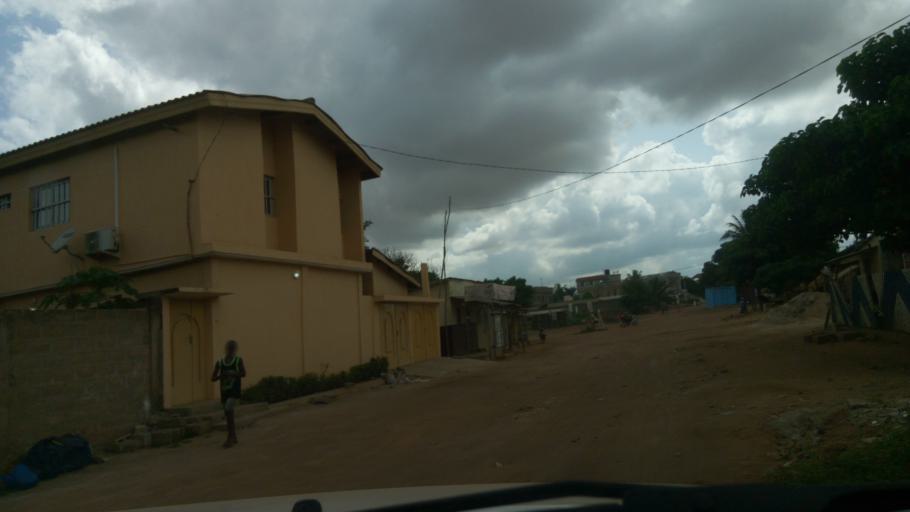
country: TG
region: Maritime
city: Lome
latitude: 6.2201
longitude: 1.1664
